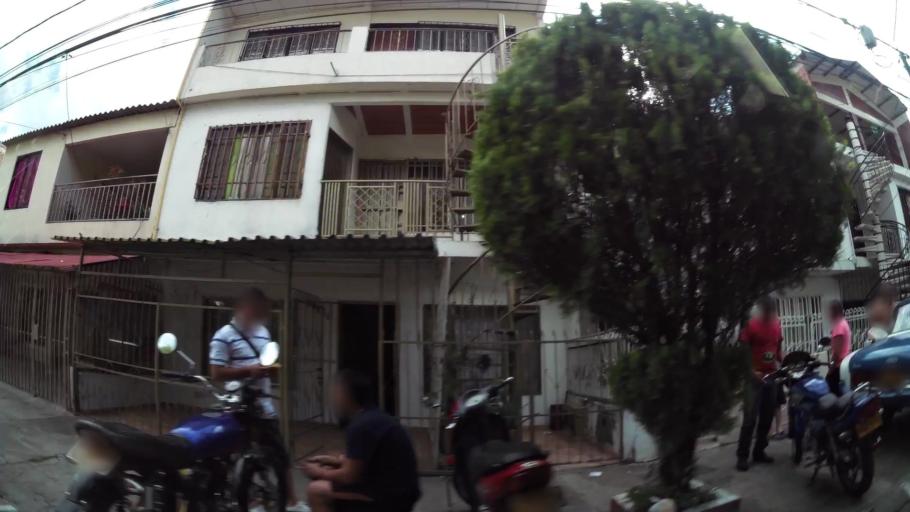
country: CO
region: Valle del Cauca
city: Cali
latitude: 3.4088
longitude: -76.5160
